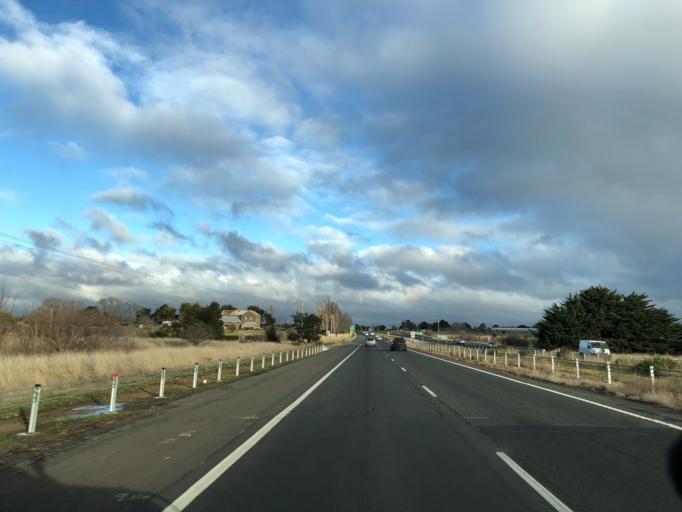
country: AU
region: Victoria
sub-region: Mount Alexander
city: Castlemaine
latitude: -37.2139
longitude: 144.4141
